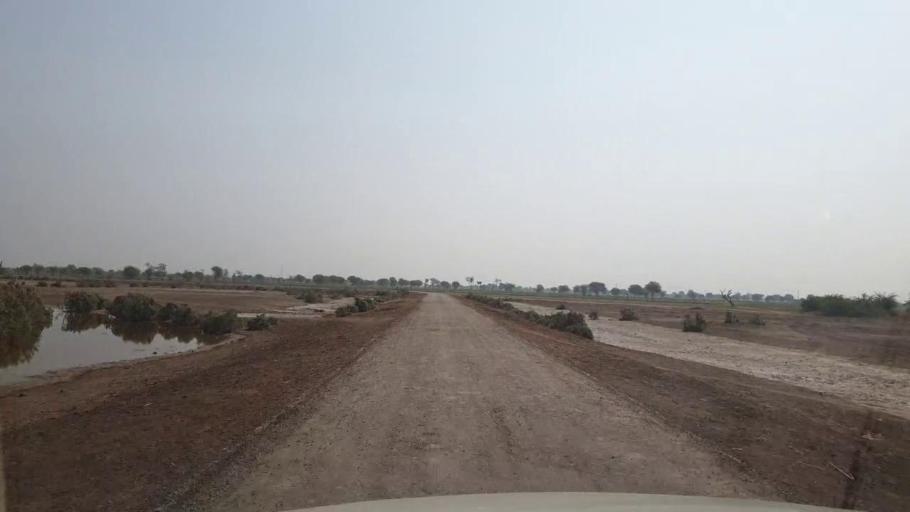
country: PK
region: Sindh
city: Chor
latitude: 25.4883
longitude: 69.7022
